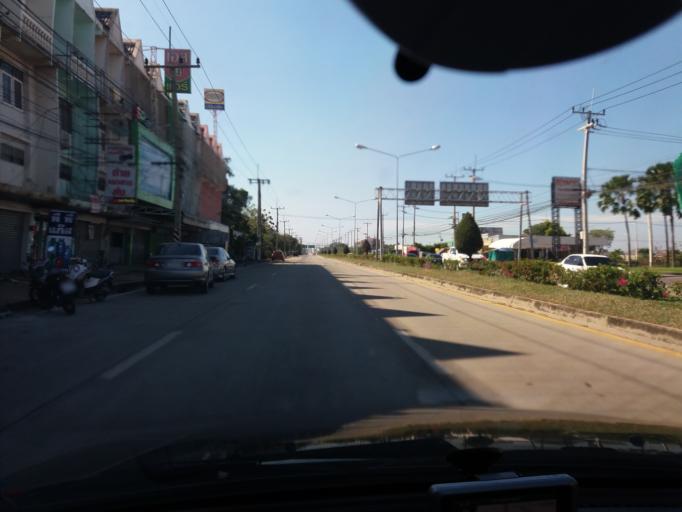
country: TH
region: Suphan Buri
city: Suphan Buri
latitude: 14.4634
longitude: 100.1401
